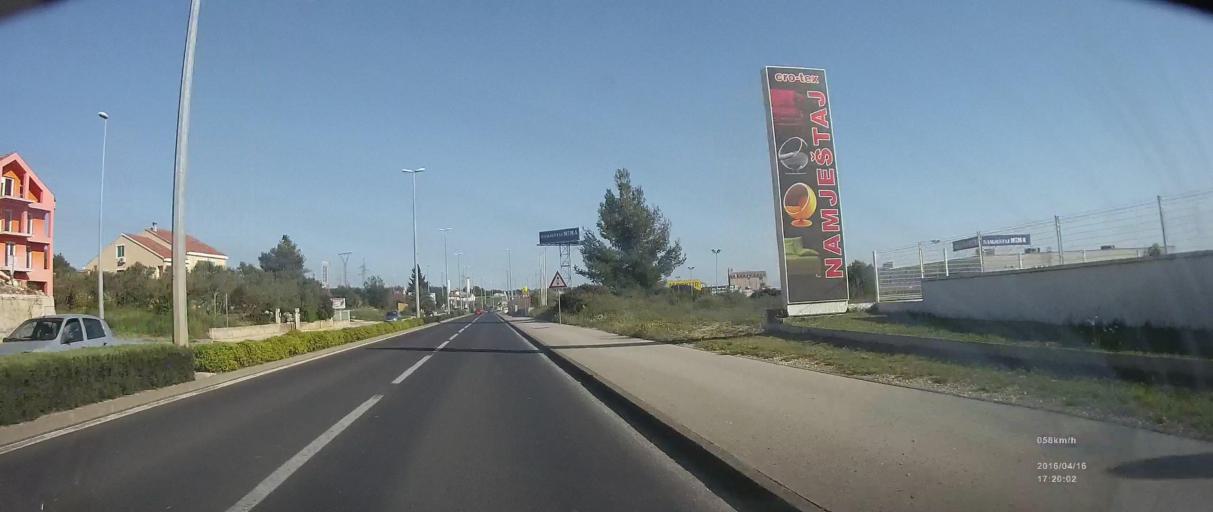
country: HR
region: Zadarska
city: Zadar
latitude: 44.1009
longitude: 15.2671
